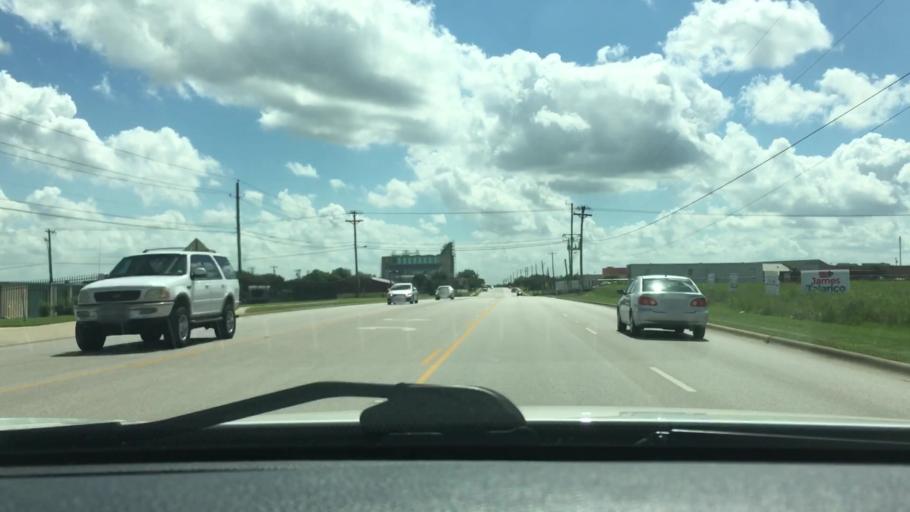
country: US
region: Texas
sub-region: Williamson County
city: Round Rock
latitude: 30.5506
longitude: -97.6761
